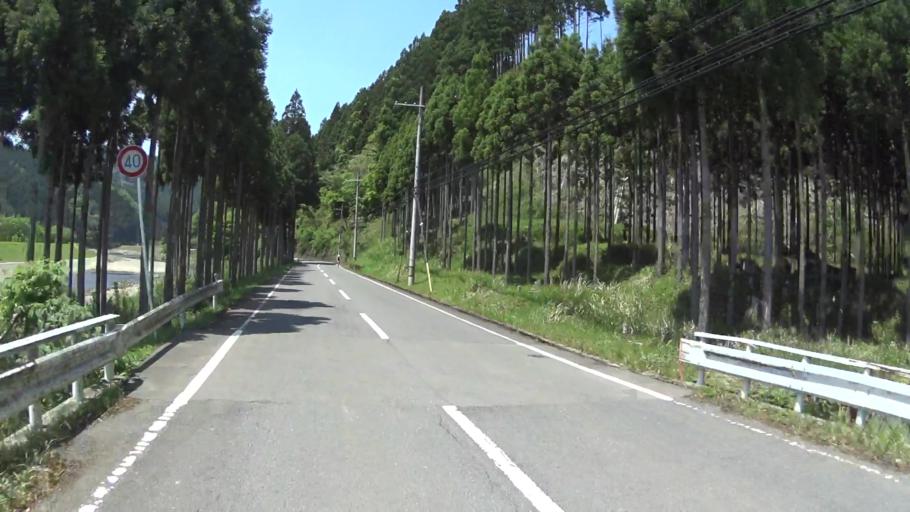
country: JP
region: Kyoto
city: Kameoka
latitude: 35.1393
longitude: 135.6013
